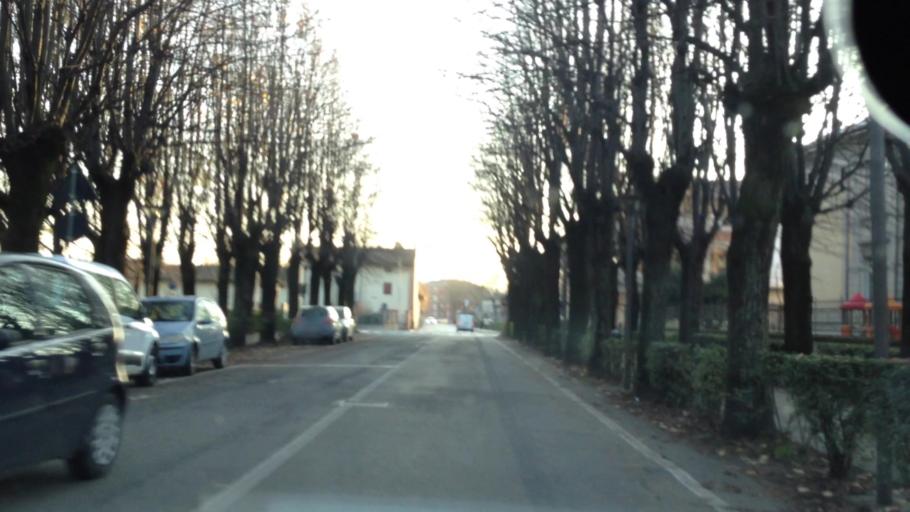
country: IT
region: Piedmont
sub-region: Provincia di Vercelli
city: Crescentino
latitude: 45.1921
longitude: 8.1063
